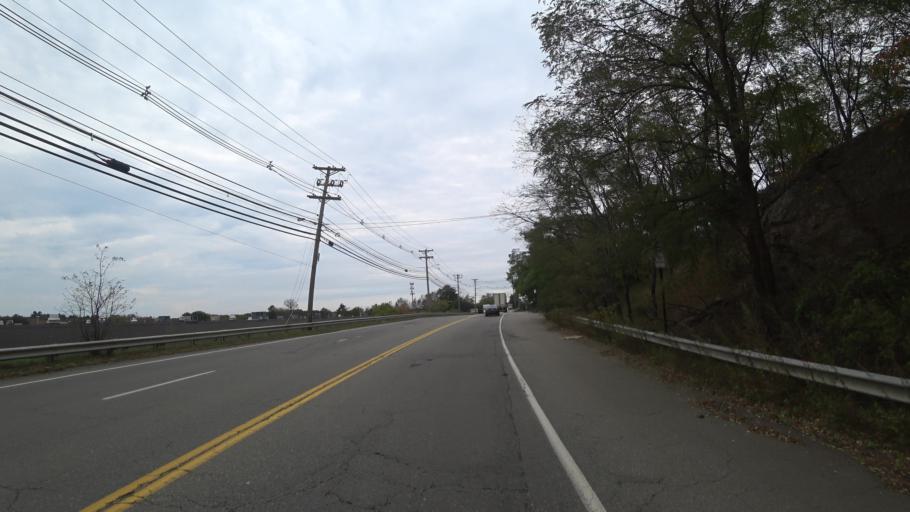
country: US
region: Massachusetts
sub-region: Middlesex County
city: Wilmington
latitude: 42.5917
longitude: -71.1606
